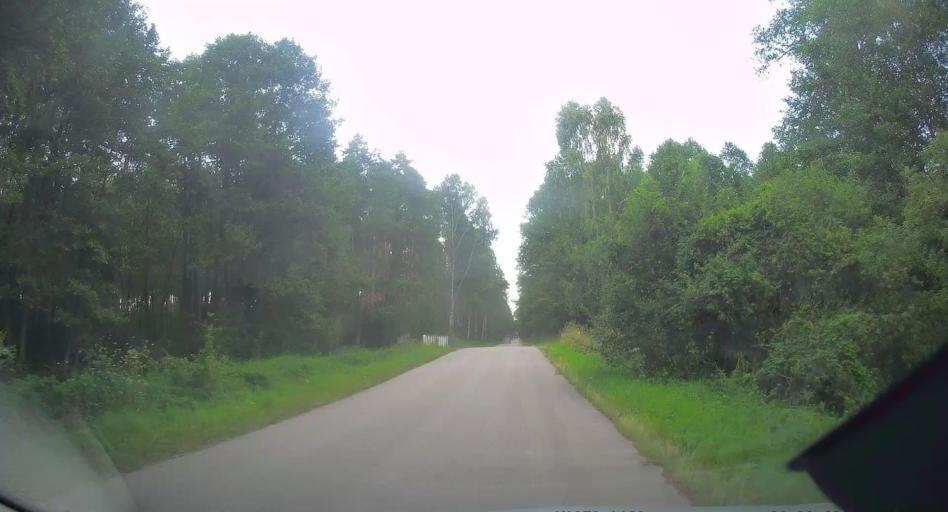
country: PL
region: Swietokrzyskie
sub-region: Powiat konecki
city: Ruda Maleniecka
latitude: 51.1393
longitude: 20.2430
